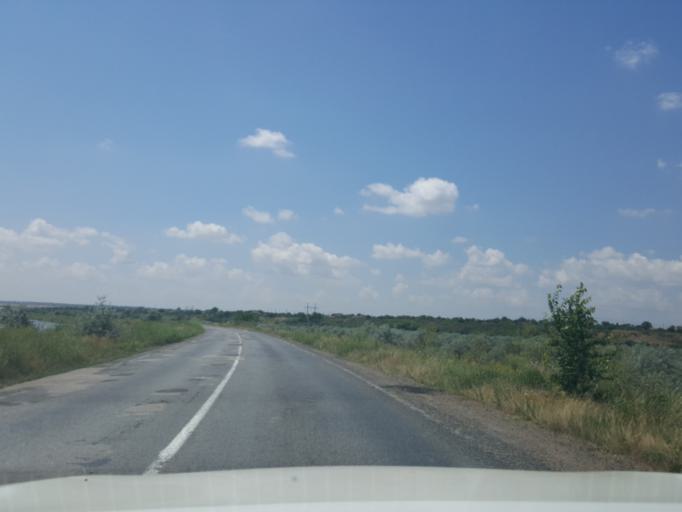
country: UA
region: Odessa
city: Bilyayivka
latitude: 46.4115
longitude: 30.1124
